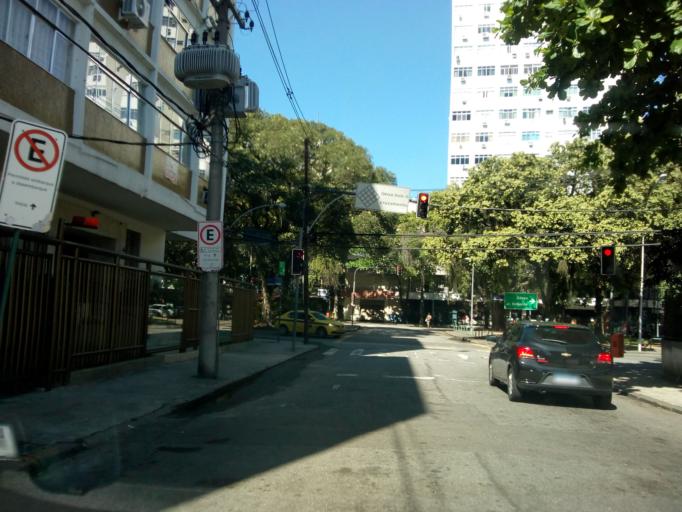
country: BR
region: Rio de Janeiro
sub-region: Rio De Janeiro
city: Rio de Janeiro
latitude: -22.9803
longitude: -43.2235
